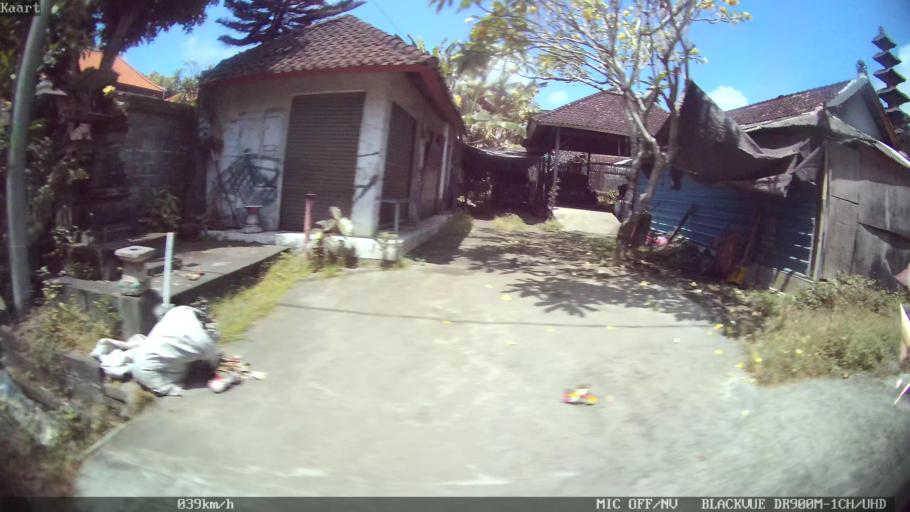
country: ID
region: Bali
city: Banjar Jabejero
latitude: -8.5922
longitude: 115.2647
